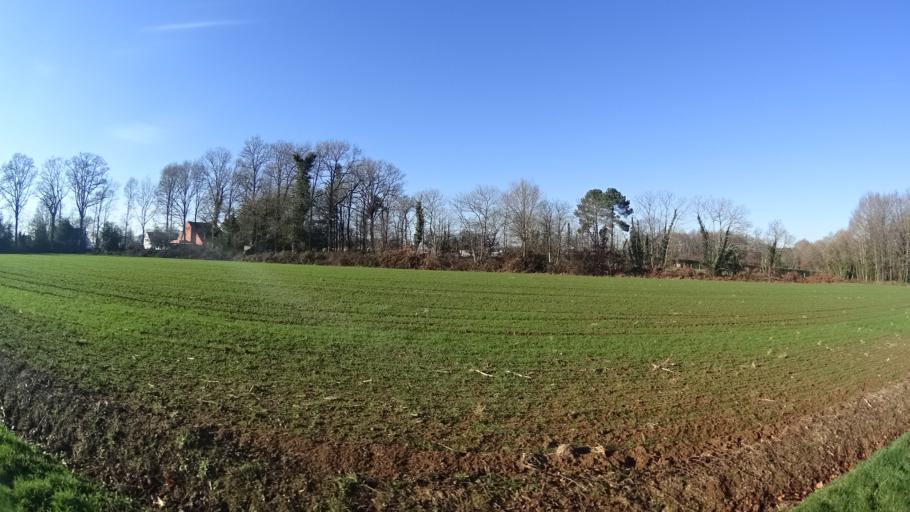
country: FR
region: Brittany
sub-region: Departement du Morbihan
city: Saint-Jean-la-Poterie
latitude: 47.6459
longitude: -2.1317
